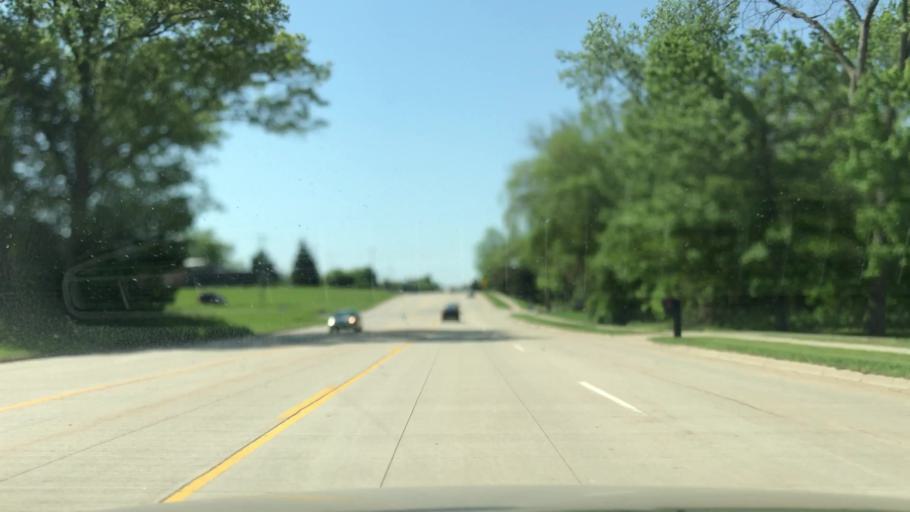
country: US
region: Michigan
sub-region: Kent County
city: East Grand Rapids
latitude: 42.9166
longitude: -85.5493
